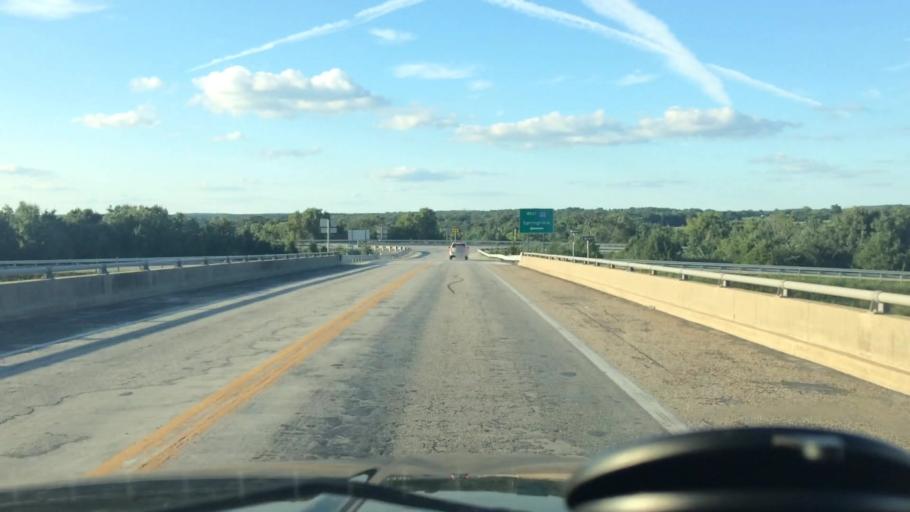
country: US
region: Missouri
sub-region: Webster County
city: Marshfield
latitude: 37.3012
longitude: -92.9995
